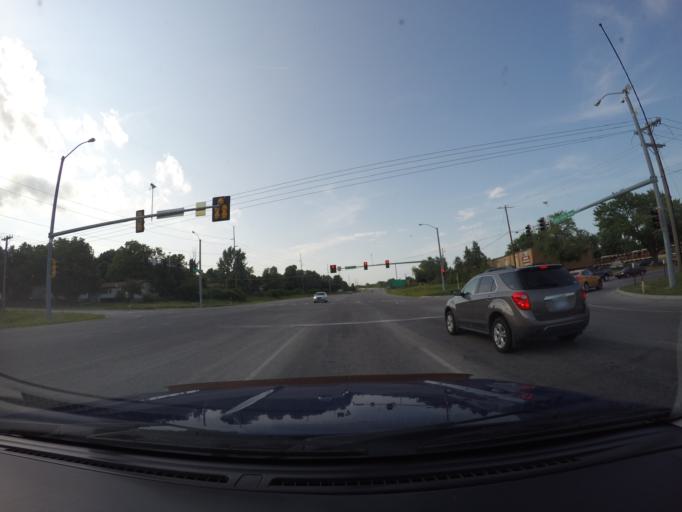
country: US
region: Kansas
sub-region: Riley County
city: Manhattan
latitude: 39.1925
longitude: -96.6123
